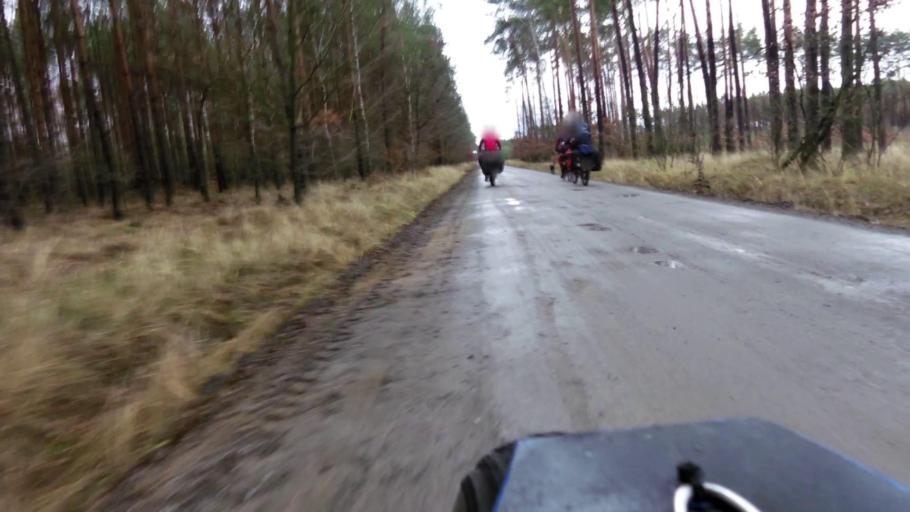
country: PL
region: Lubusz
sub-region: Powiat gorzowski
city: Witnica
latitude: 52.7013
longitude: 14.8355
